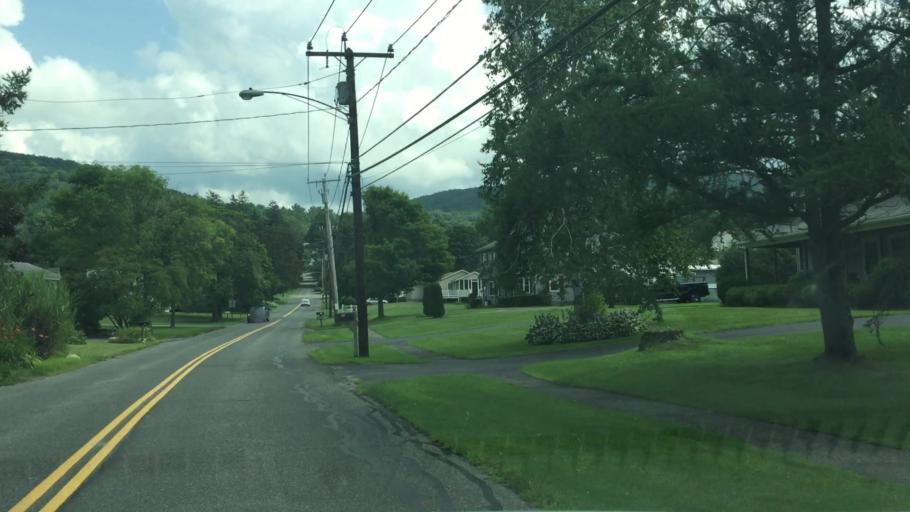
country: US
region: Massachusetts
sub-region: Berkshire County
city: Lee
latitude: 42.3133
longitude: -73.2369
